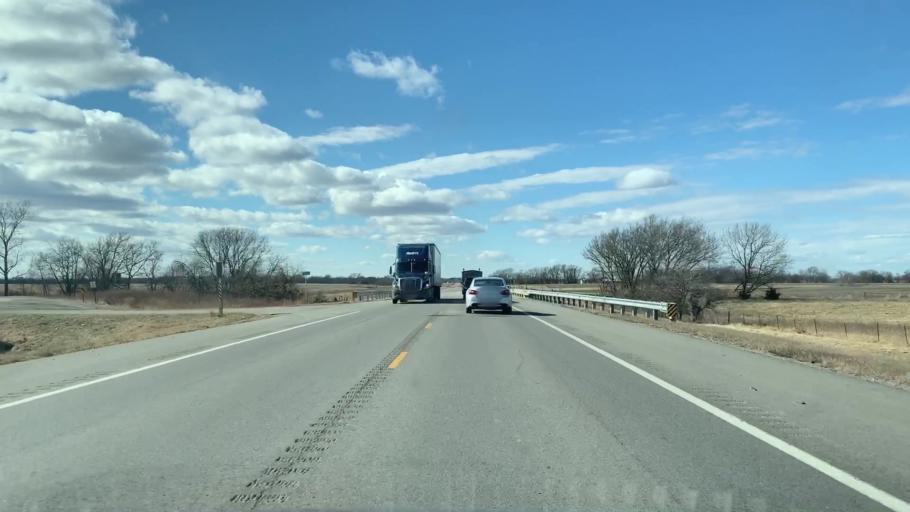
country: US
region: Kansas
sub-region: Crawford County
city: Pittsburg
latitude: 37.3396
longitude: -94.8490
